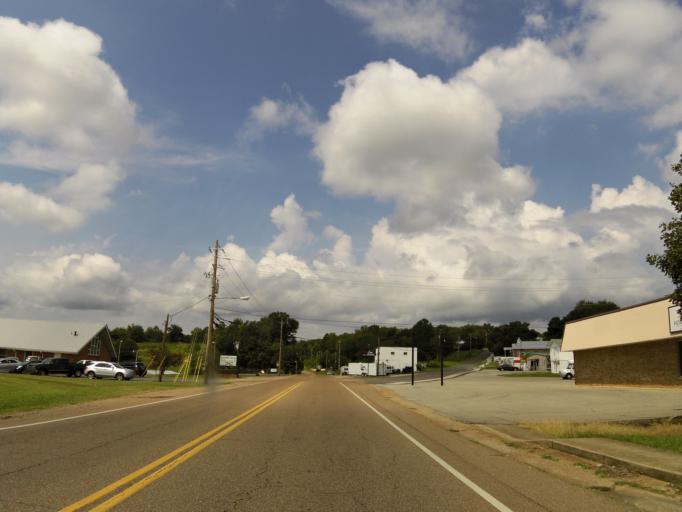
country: US
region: Tennessee
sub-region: Perry County
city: Linden
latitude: 35.6172
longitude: -87.8410
